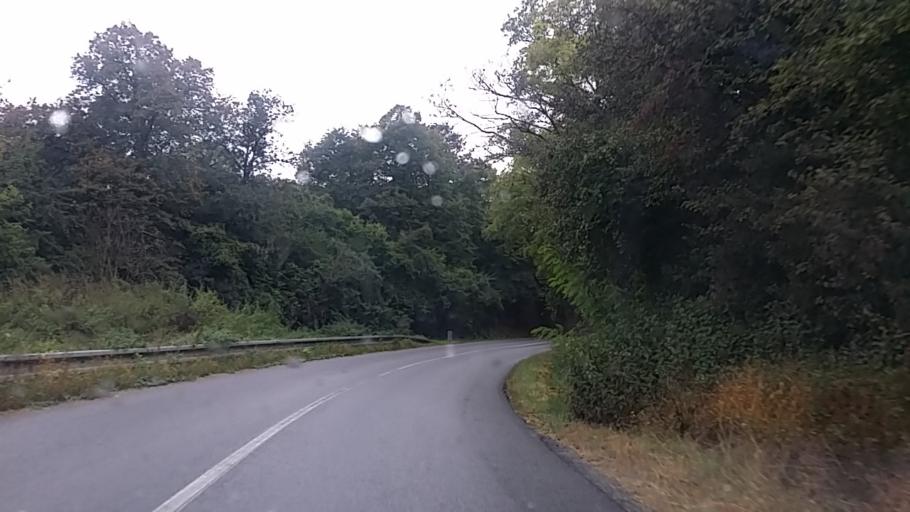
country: HU
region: Komarom-Esztergom
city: Esztergom
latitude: 47.8599
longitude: 18.7430
